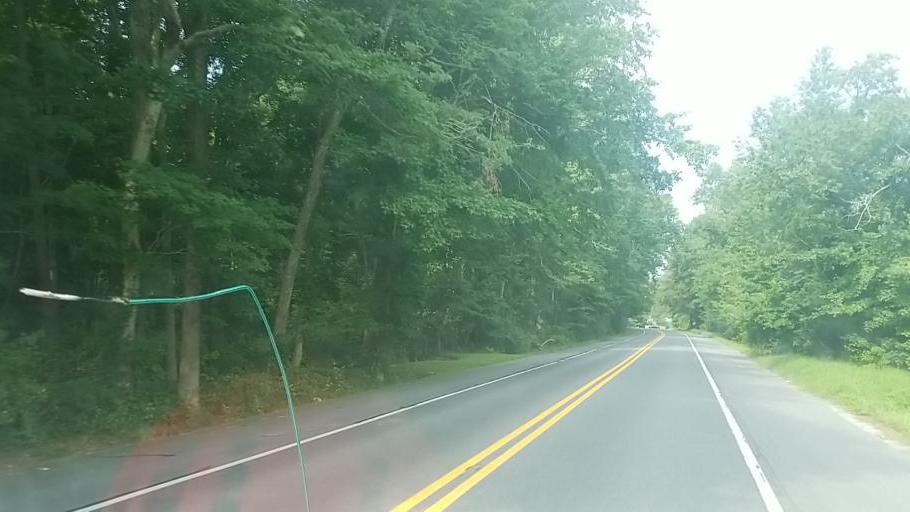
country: US
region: Delaware
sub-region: Sussex County
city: Long Neck
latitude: 38.5447
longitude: -75.1693
